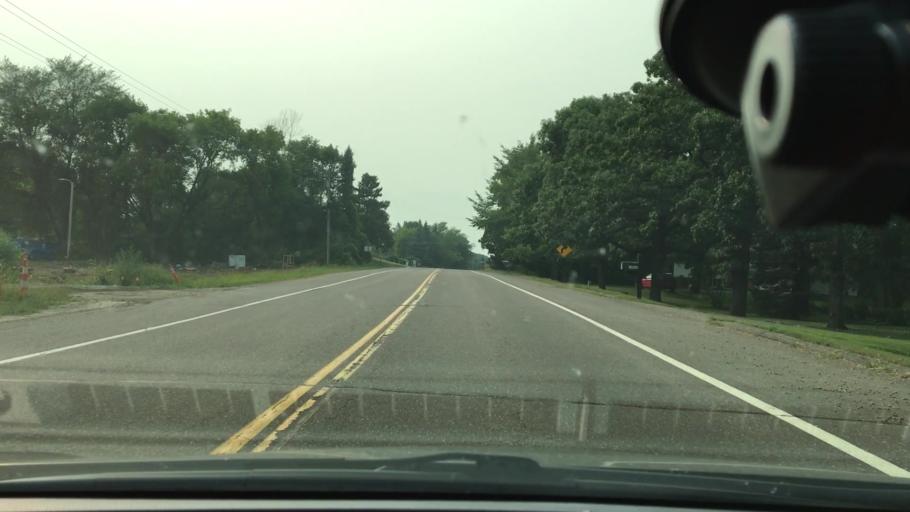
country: US
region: Minnesota
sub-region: Anoka County
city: Ramsey
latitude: 45.2088
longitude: -93.4465
